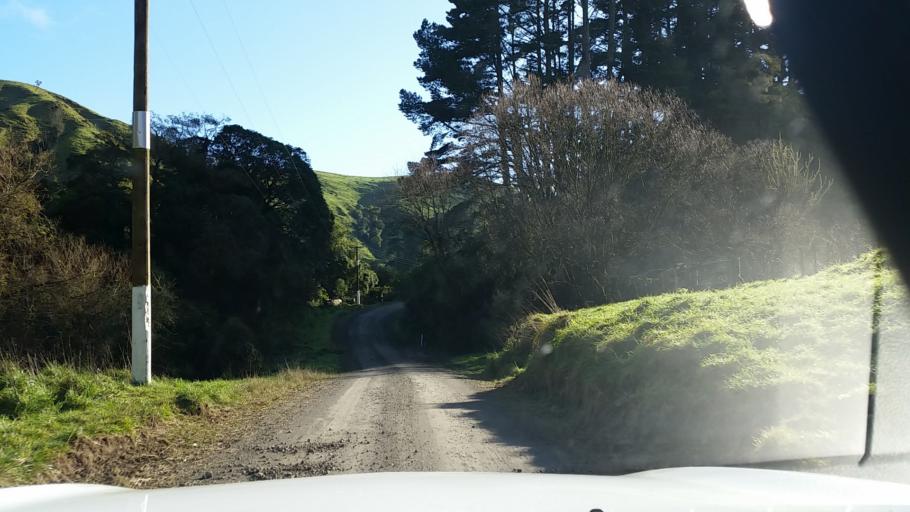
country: NZ
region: Taranaki
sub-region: South Taranaki District
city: Eltham
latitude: -39.5096
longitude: 174.3975
